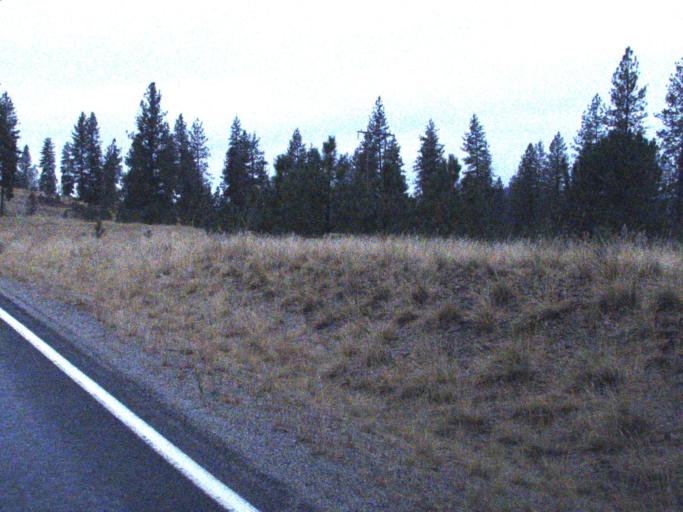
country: US
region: Washington
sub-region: Spokane County
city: Fairchild Air Force Base
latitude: 47.8835
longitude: -117.8389
